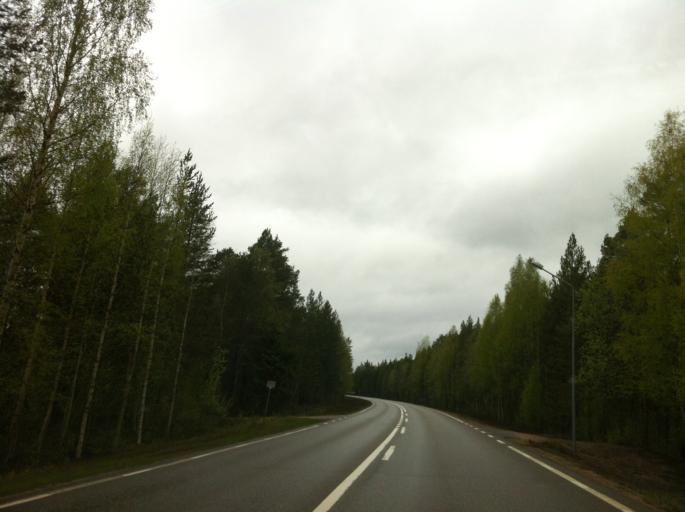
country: SE
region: Jaemtland
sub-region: Harjedalens Kommun
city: Sveg
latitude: 62.1345
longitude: 14.0501
